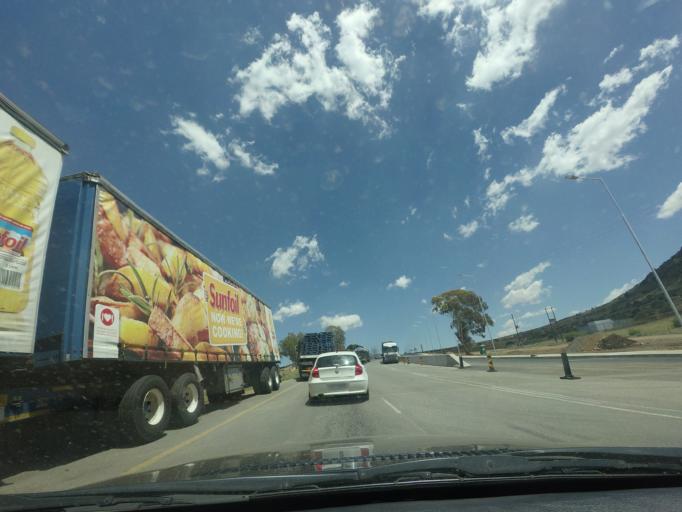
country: LS
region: Maseru
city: Maseru
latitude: -29.2974
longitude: 27.4465
